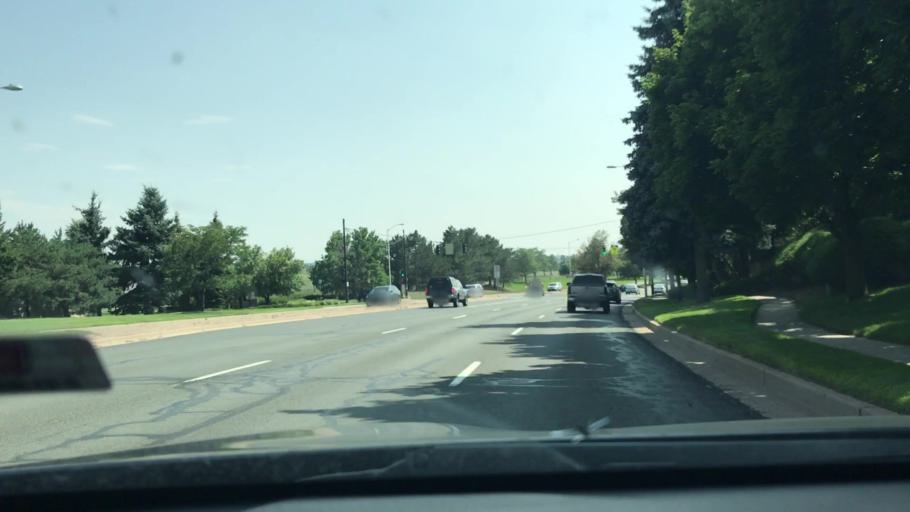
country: US
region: Colorado
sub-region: El Paso County
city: Black Forest
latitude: 38.9537
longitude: -104.7645
